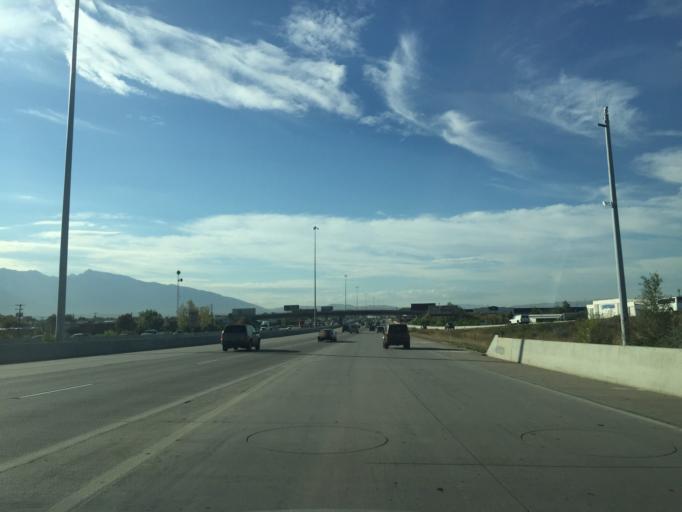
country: US
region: Utah
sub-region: Salt Lake County
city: South Salt Lake
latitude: 40.7157
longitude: -111.9048
